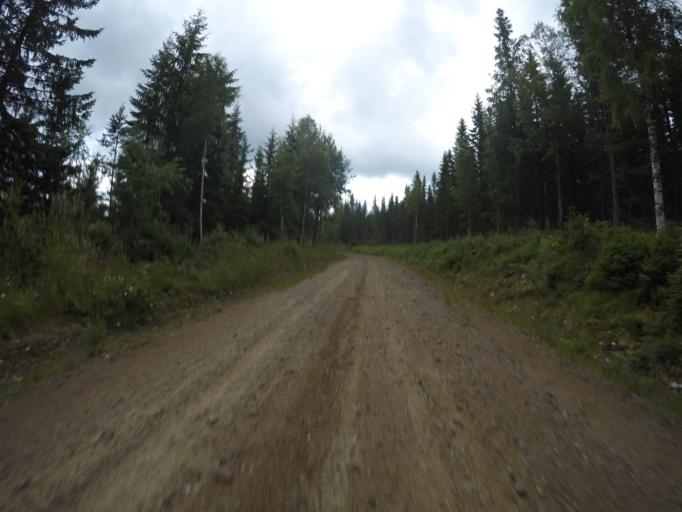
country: SE
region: Vaermland
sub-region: Filipstads Kommun
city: Lesjofors
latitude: 60.1979
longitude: 14.3591
